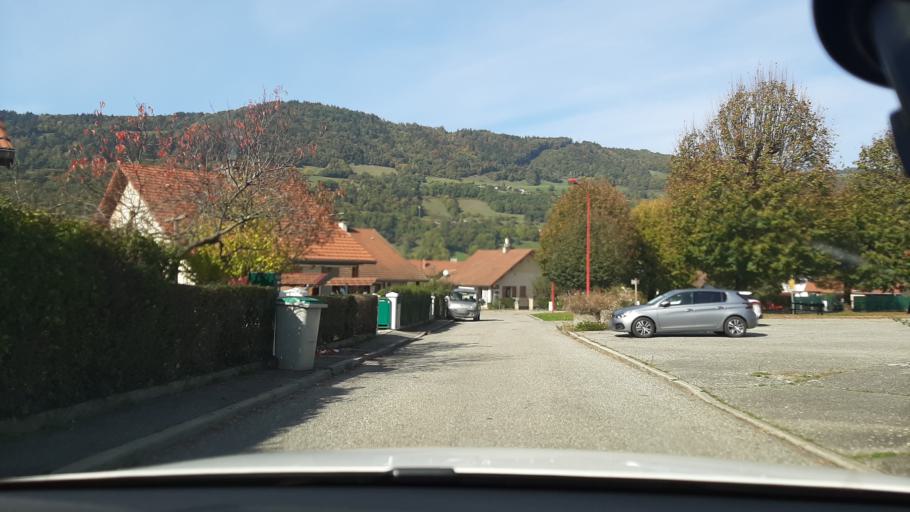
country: FR
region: Rhone-Alpes
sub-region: Departement de la Savoie
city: La Rochette
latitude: 45.4518
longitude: 6.1132
